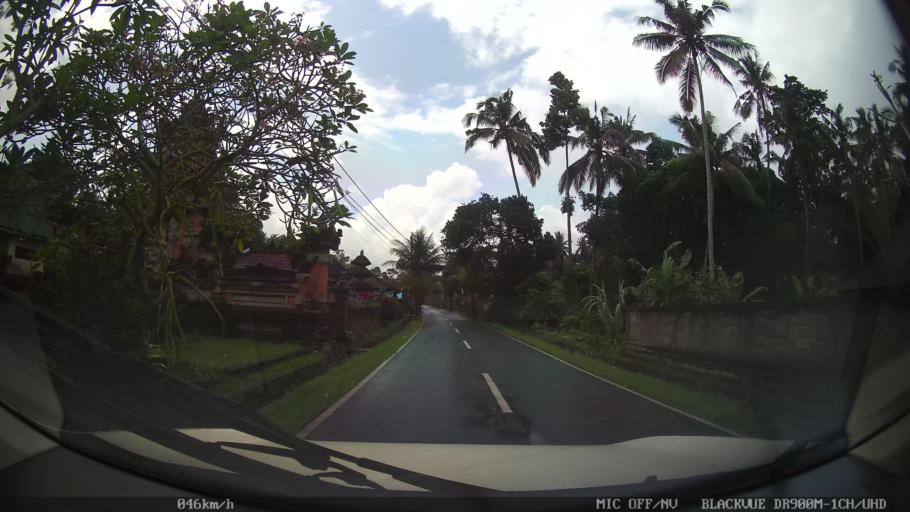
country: ID
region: Bali
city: Banjar Teguan
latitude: -8.4980
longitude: 115.2348
